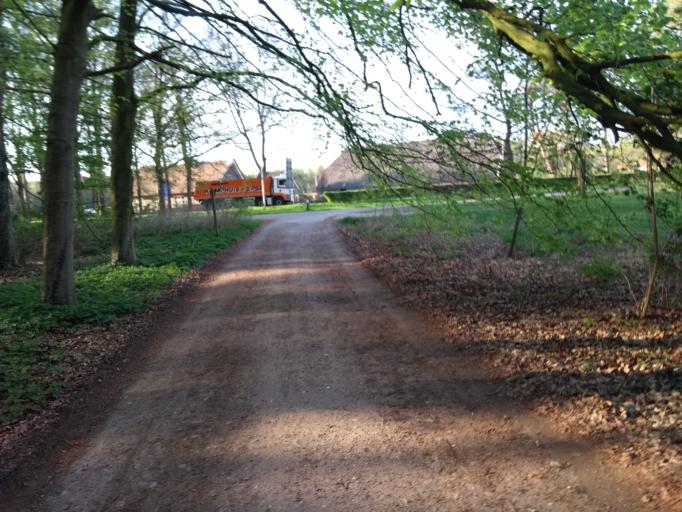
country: NL
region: Gelderland
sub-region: Gemeente Lochem
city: Barchem
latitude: 52.0790
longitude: 6.4430
